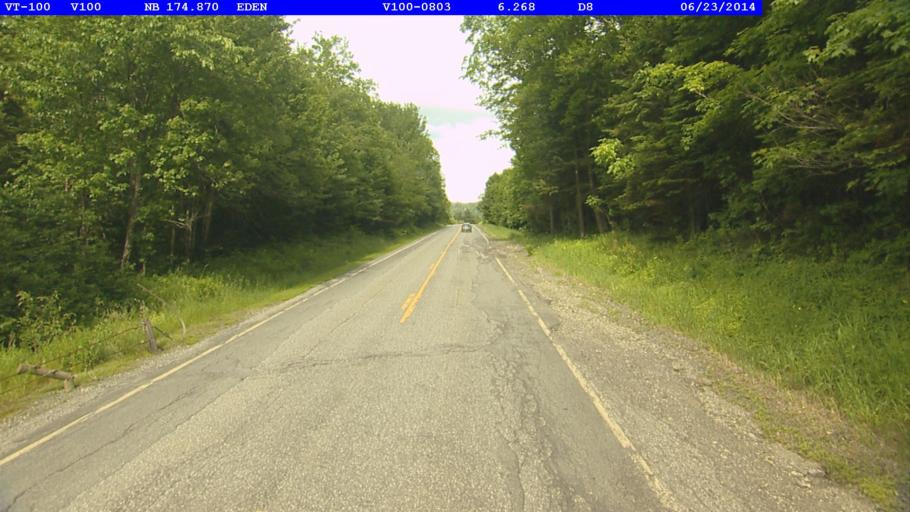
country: US
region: Vermont
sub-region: Lamoille County
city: Hyde Park
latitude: 44.7305
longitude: -72.4891
